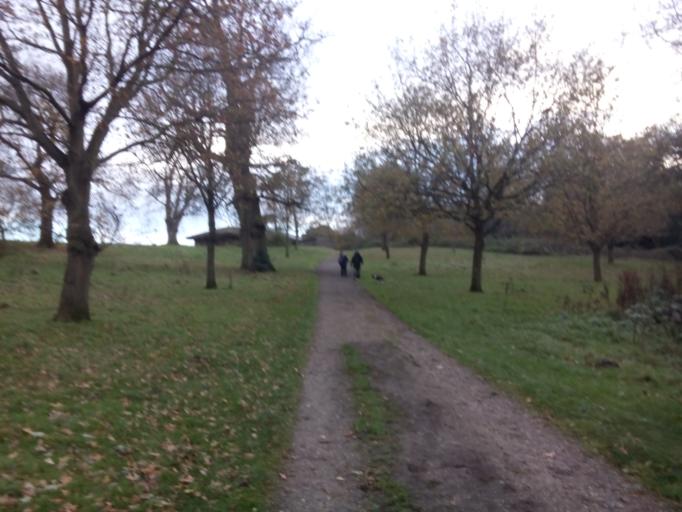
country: GB
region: England
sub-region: Suffolk
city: Bramford
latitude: 52.0523
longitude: 1.1159
